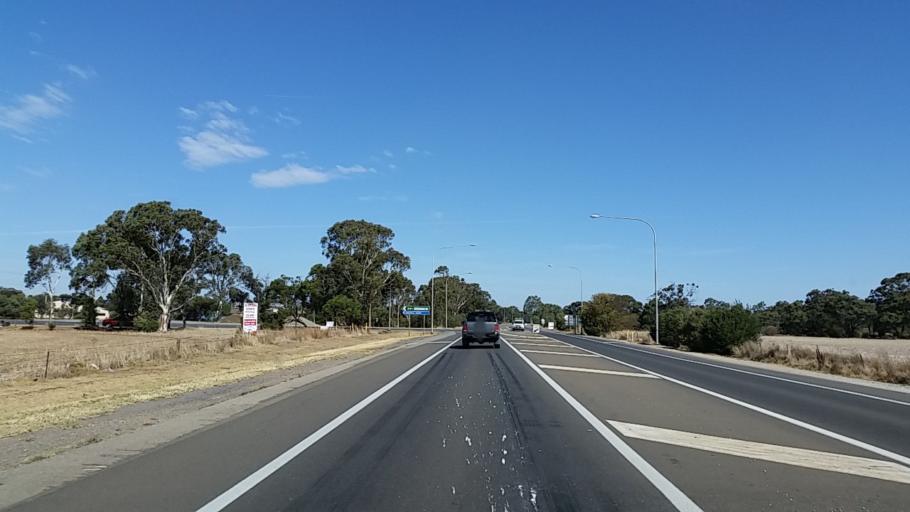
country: AU
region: South Australia
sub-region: Light
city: Willaston
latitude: -34.5654
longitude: 138.7465
